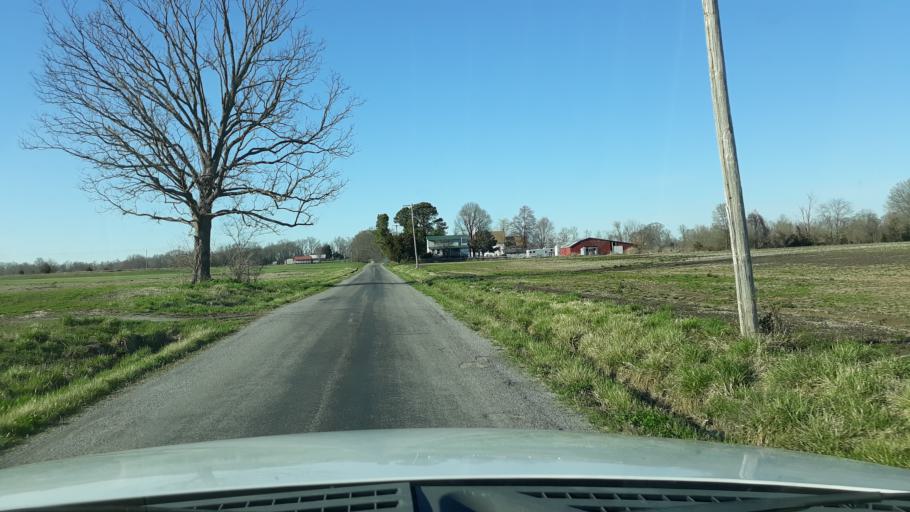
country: US
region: Illinois
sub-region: Saline County
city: Harrisburg
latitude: 37.8020
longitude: -88.6055
